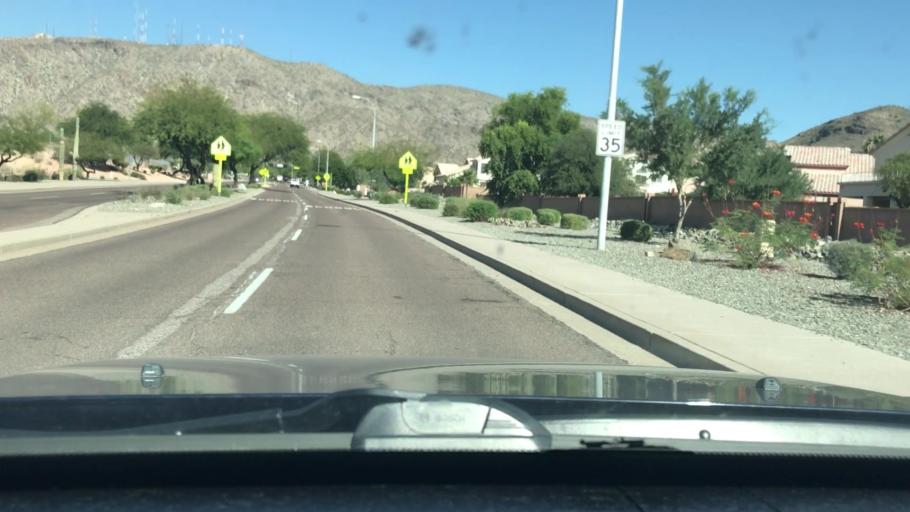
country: US
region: Arizona
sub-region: Maricopa County
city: Guadalupe
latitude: 33.3096
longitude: -112.0549
